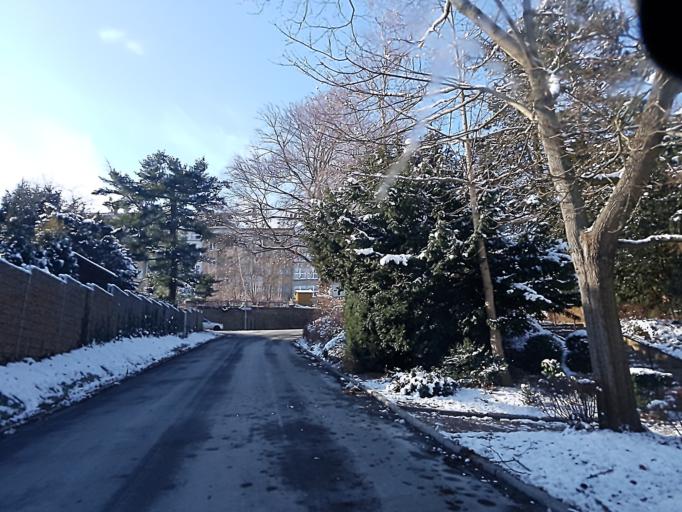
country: DE
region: Saxony
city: Leisnig
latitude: 51.1565
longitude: 12.9290
